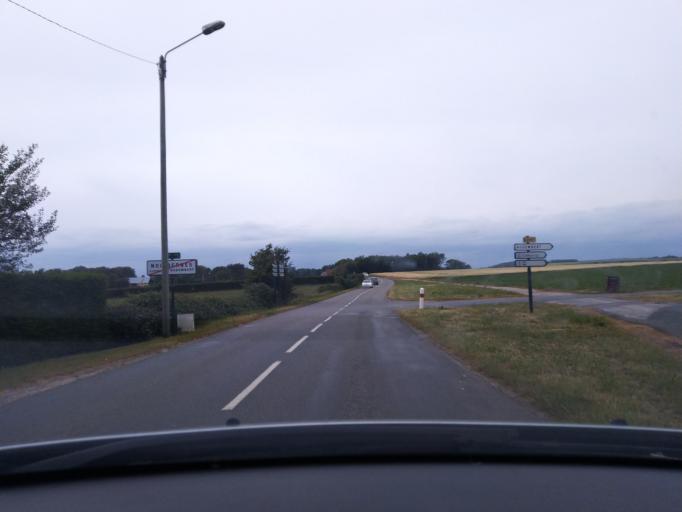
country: FR
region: Nord-Pas-de-Calais
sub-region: Departement du Pas-de-Calais
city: Wissant
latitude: 50.8461
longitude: 1.6796
